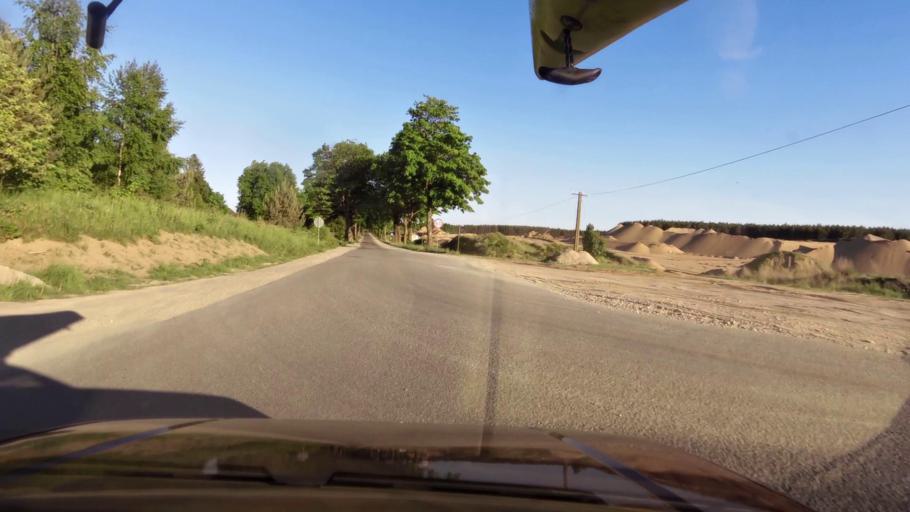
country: PL
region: West Pomeranian Voivodeship
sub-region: Powiat szczecinecki
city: Bialy Bor
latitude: 53.9388
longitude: 16.7903
